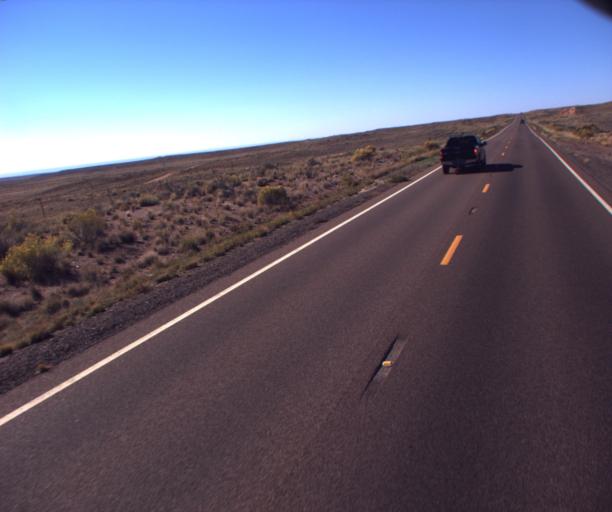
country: US
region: Arizona
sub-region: Navajo County
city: Joseph City
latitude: 35.1660
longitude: -110.4519
